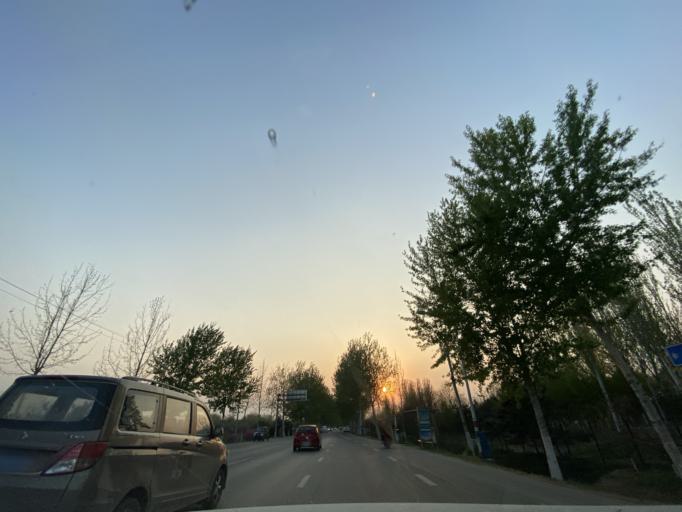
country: CN
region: Beijing
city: Weishanzhuang
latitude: 39.6149
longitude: 116.3957
